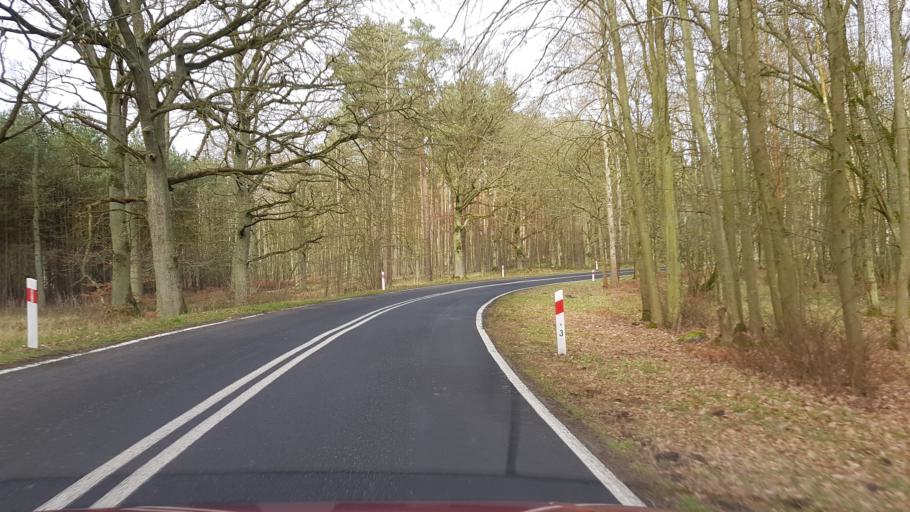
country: PL
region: West Pomeranian Voivodeship
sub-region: Powiat policki
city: Nowe Warpno
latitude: 53.6830
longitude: 14.3539
